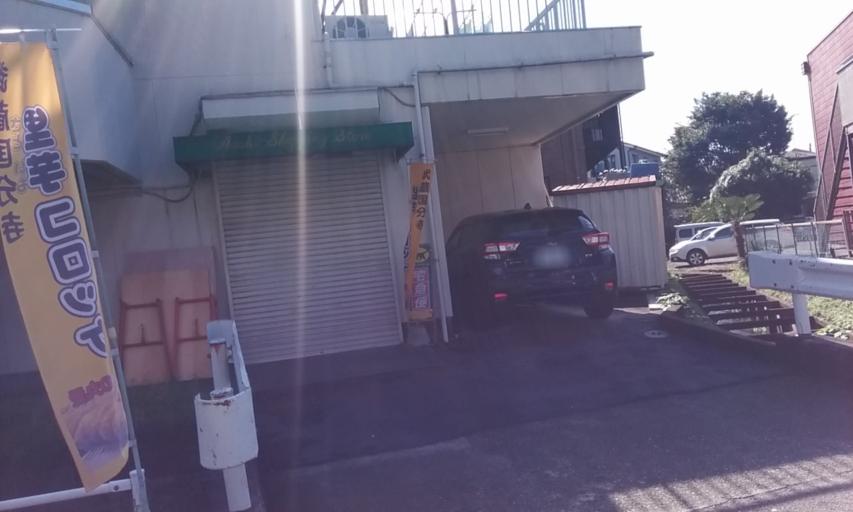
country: JP
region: Tokyo
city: Kokubunji
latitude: 35.6961
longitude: 139.4805
